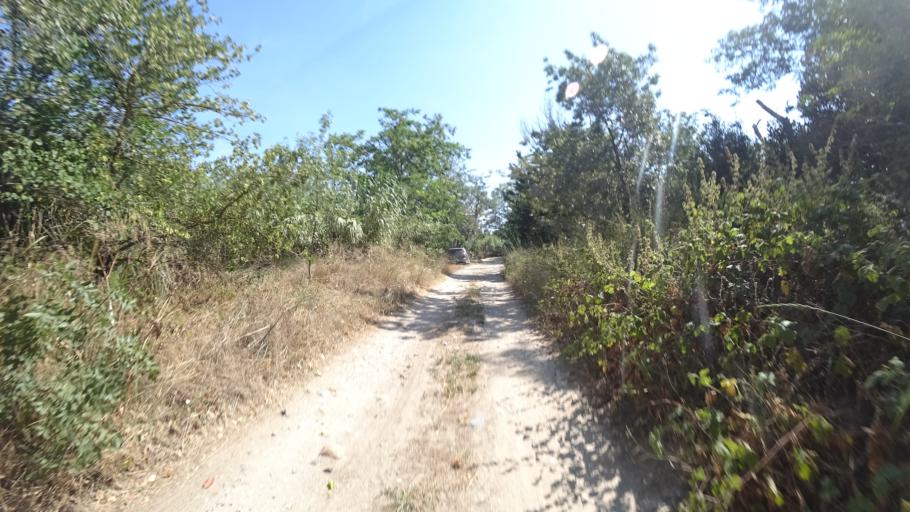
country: FR
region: Languedoc-Roussillon
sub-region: Departement des Pyrenees-Orientales
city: Rivesaltes
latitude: 42.7739
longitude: 2.8573
